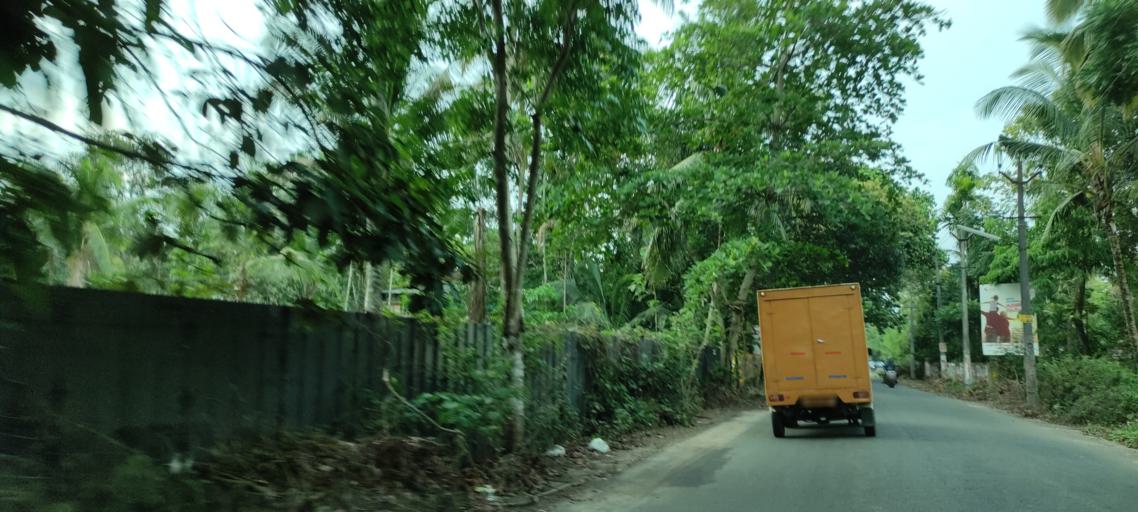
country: IN
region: Kerala
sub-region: Kottayam
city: Vaikam
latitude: 9.7659
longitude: 76.3627
